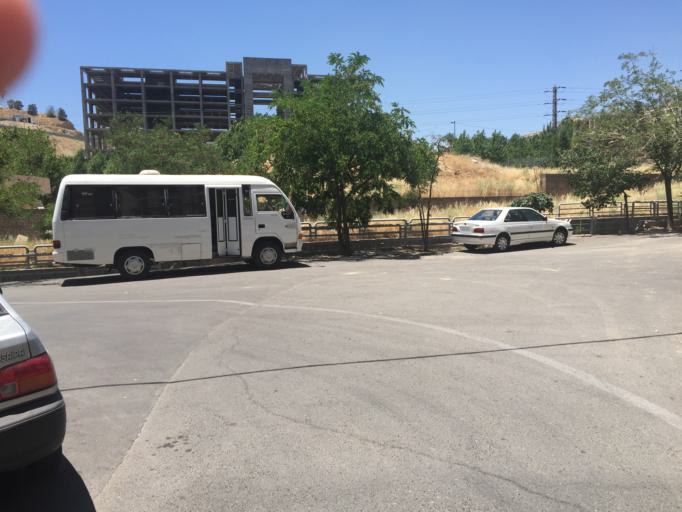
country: IR
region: Tehran
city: Tajrish
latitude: 35.7543
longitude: 51.4382
